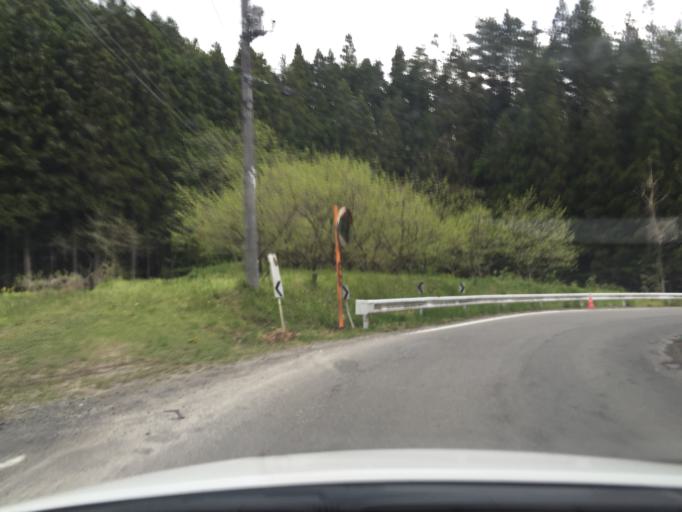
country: JP
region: Fukushima
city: Hobaramachi
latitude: 37.7250
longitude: 140.6405
